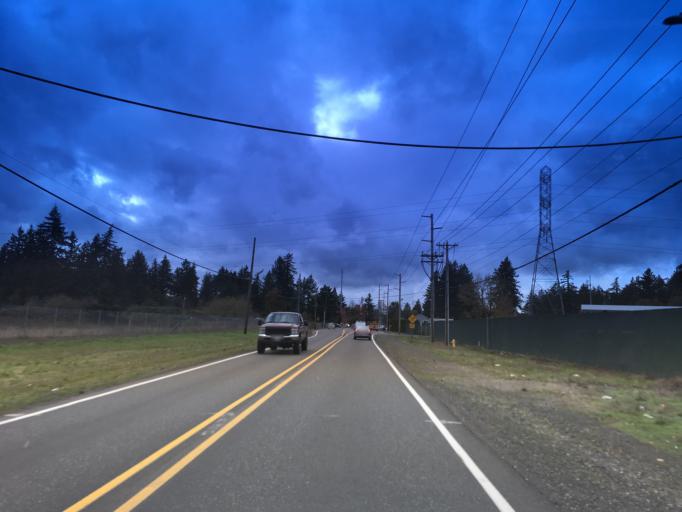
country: US
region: Oregon
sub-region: Multnomah County
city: Fairview
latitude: 45.5275
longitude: -122.4518
